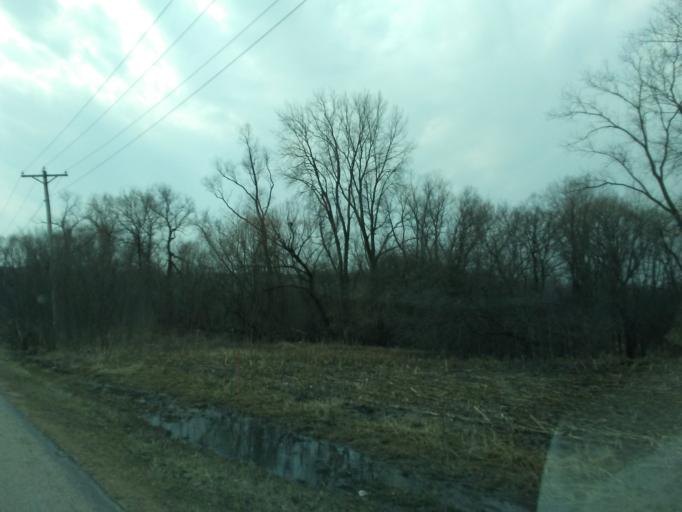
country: US
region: Wisconsin
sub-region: Dane County
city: Middleton
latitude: 43.1194
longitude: -89.4915
